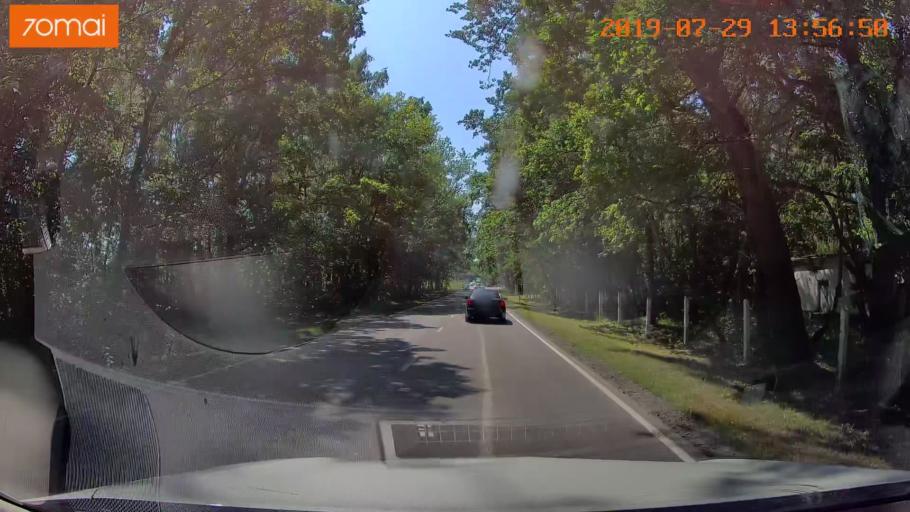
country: RU
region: Kaliningrad
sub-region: Gorod Kaliningrad
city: Baltiysk
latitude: 54.7056
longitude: 19.9463
